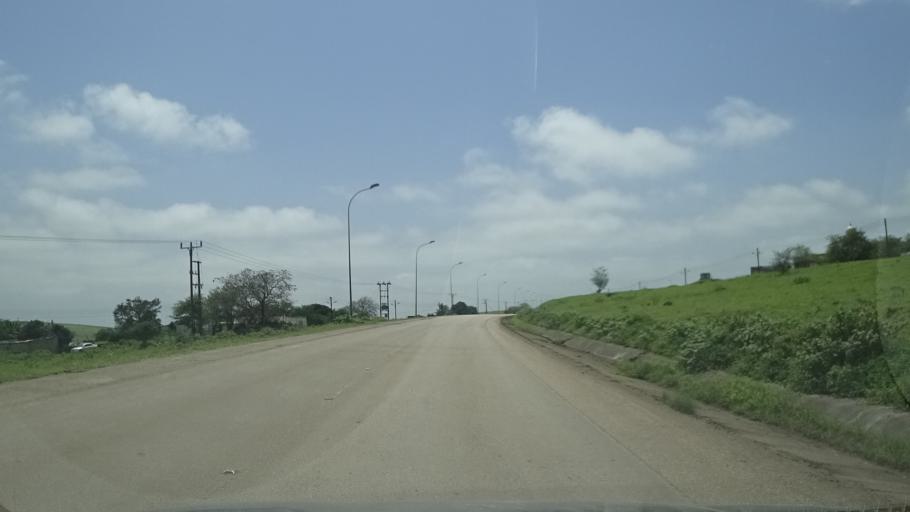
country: OM
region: Zufar
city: Salalah
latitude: 17.1778
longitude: 54.2507
